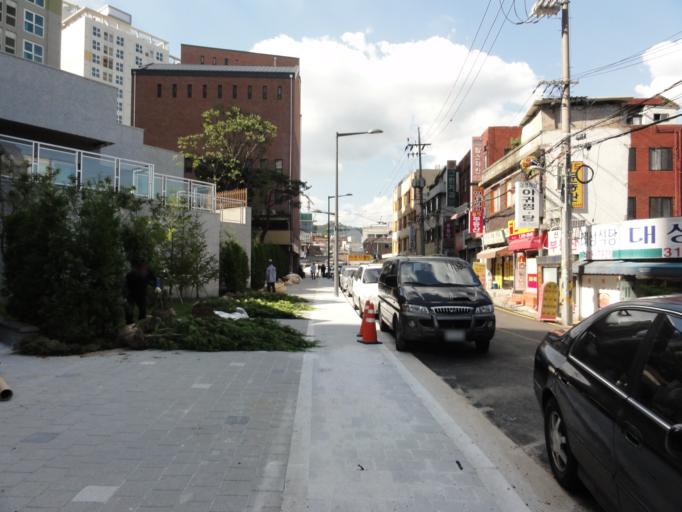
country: KR
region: Seoul
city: Seoul
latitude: 37.5546
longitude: 126.9555
